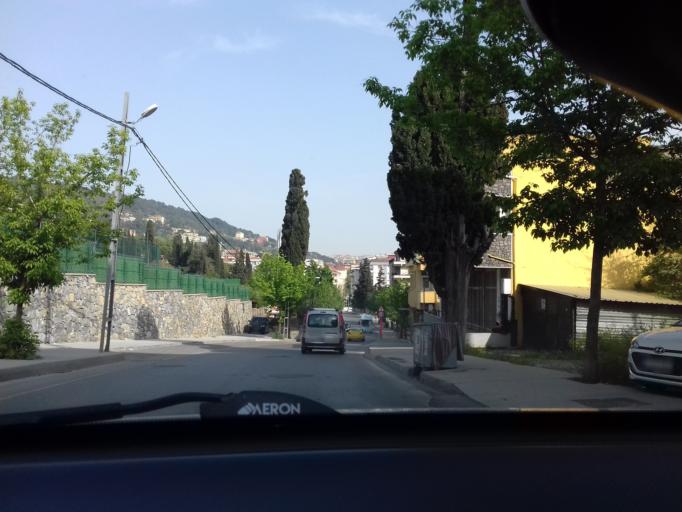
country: TR
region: Istanbul
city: Pendik
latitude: 40.9142
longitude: 29.2244
